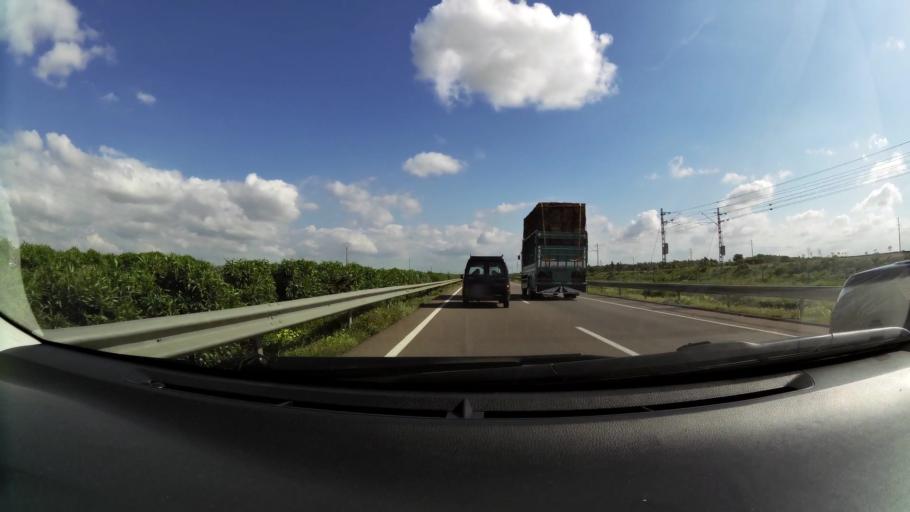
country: MA
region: Chaouia-Ouardigha
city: Nouaseur
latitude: 33.3463
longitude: -7.6143
